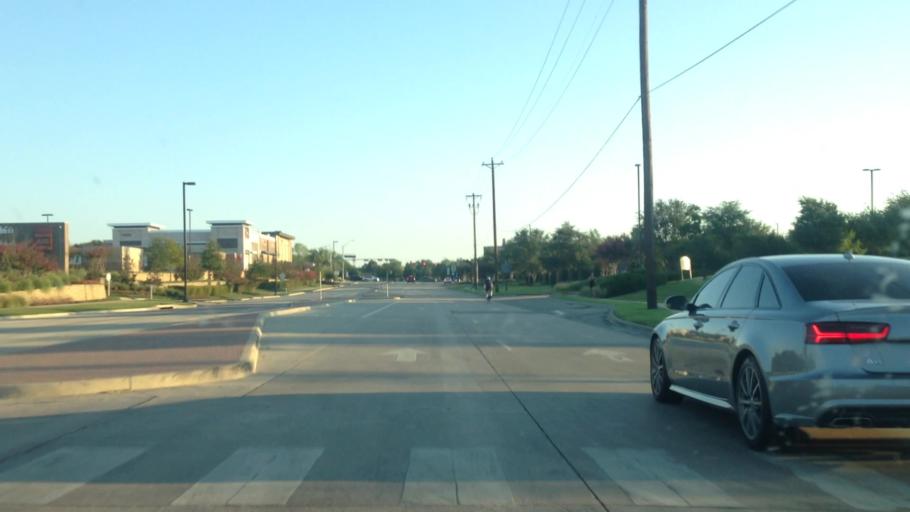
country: US
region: Texas
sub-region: Tarrant County
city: Southlake
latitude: 32.9385
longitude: -97.1336
